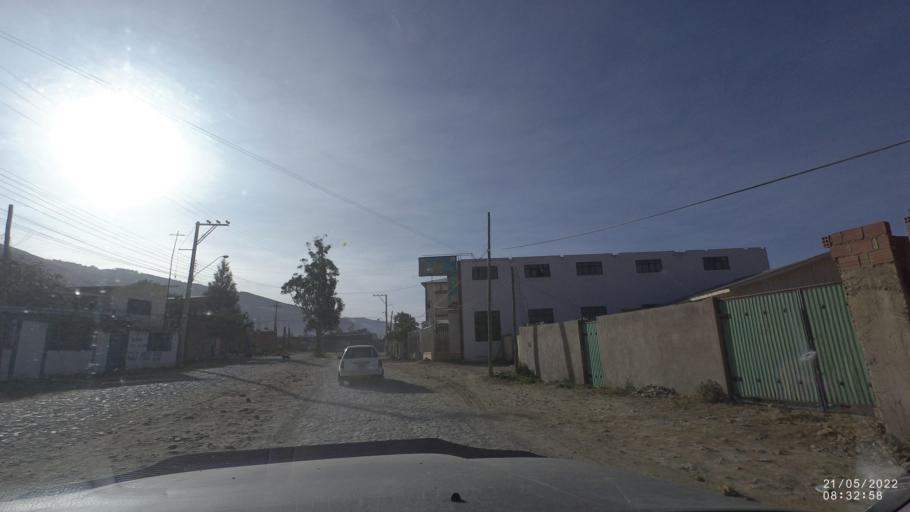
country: BO
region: Cochabamba
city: Cochabamba
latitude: -17.3859
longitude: -66.0522
